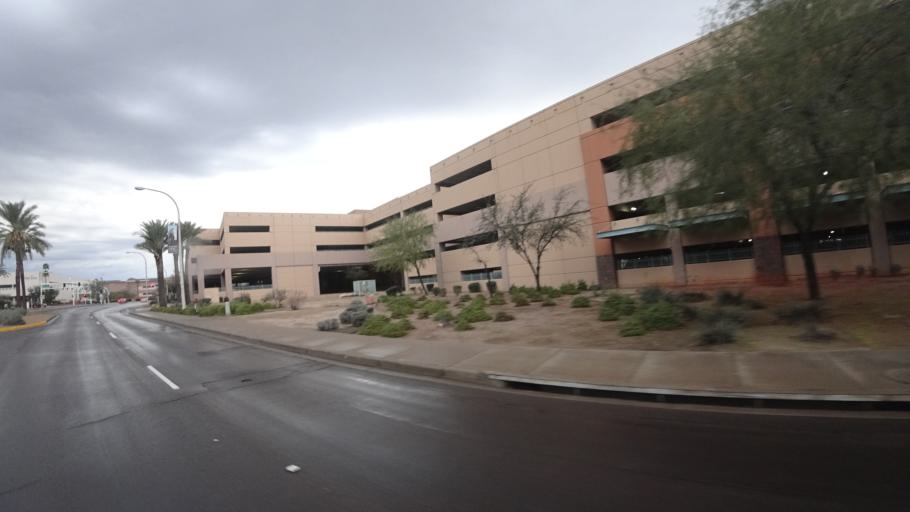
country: US
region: Arizona
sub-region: Maricopa County
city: Scottsdale
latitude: 33.5006
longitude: -111.9303
